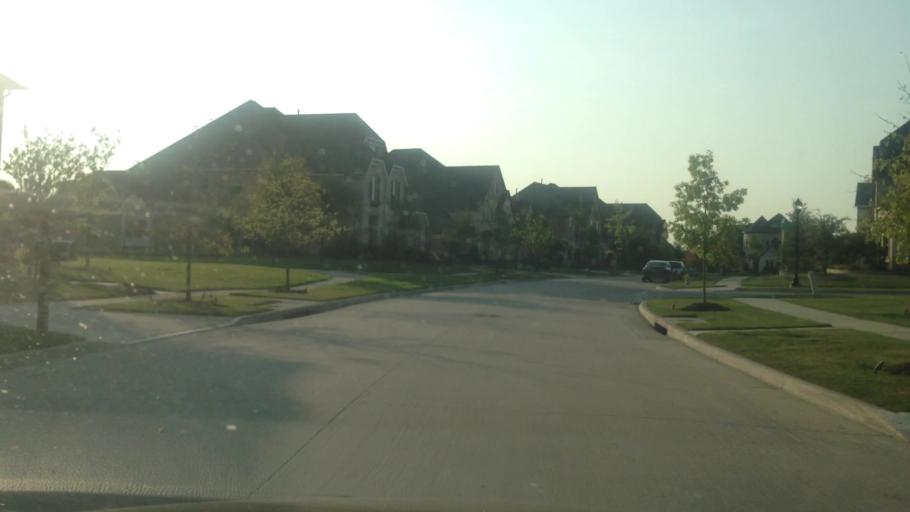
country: US
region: Texas
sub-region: Denton County
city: The Colony
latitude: 33.1358
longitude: -96.8740
